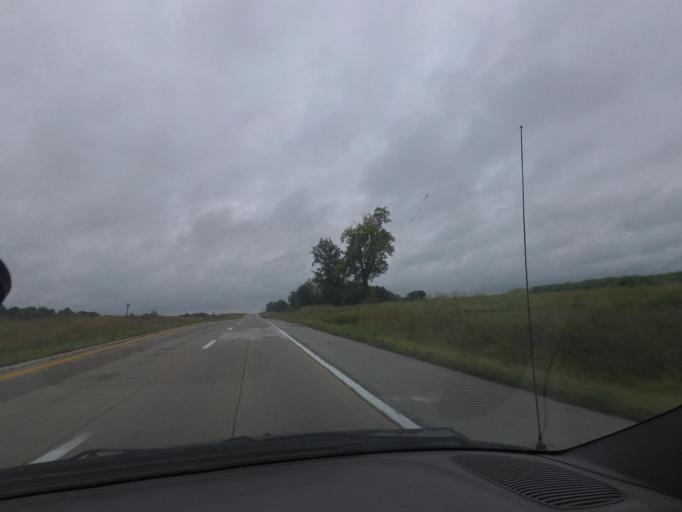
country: US
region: Missouri
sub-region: Marion County
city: Monroe City
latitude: 39.6581
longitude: -91.7741
